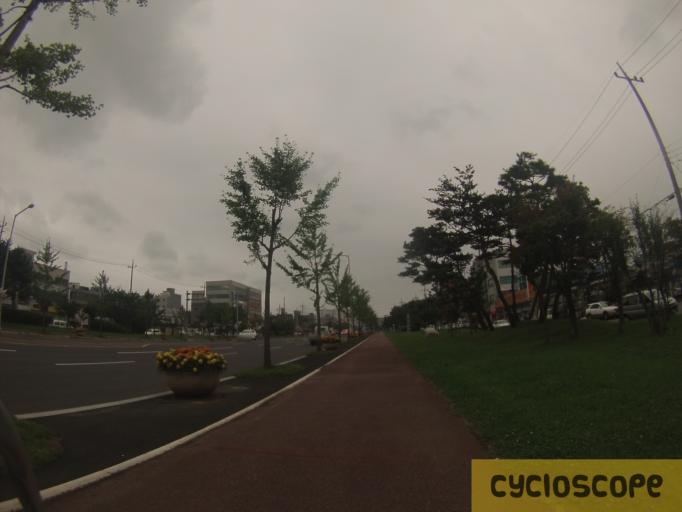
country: KR
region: Chungcheongnam-do
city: Taisen-ri
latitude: 36.4207
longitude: 126.7105
